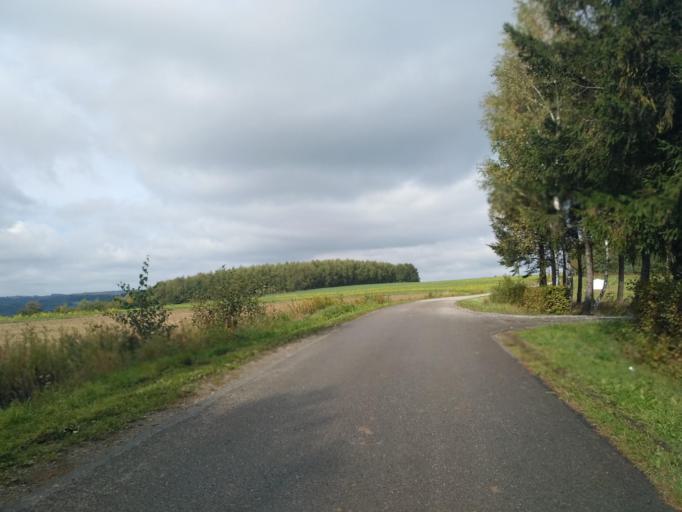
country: PL
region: Subcarpathian Voivodeship
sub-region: Powiat ropczycko-sedziszowski
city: Niedzwiada
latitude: 49.9300
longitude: 21.5034
